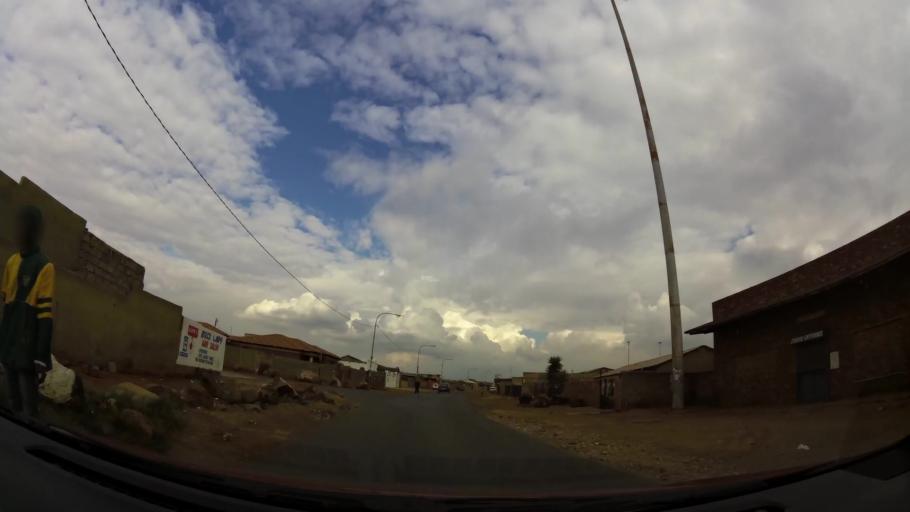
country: ZA
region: Gauteng
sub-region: City of Johannesburg Metropolitan Municipality
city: Soweto
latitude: -26.2439
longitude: 27.8505
